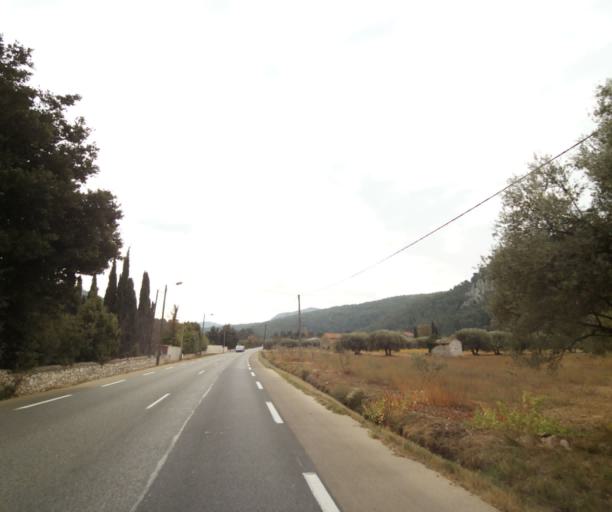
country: FR
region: Provence-Alpes-Cote d'Azur
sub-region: Departement des Bouches-du-Rhone
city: Gemenos
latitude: 43.2799
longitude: 5.6302
